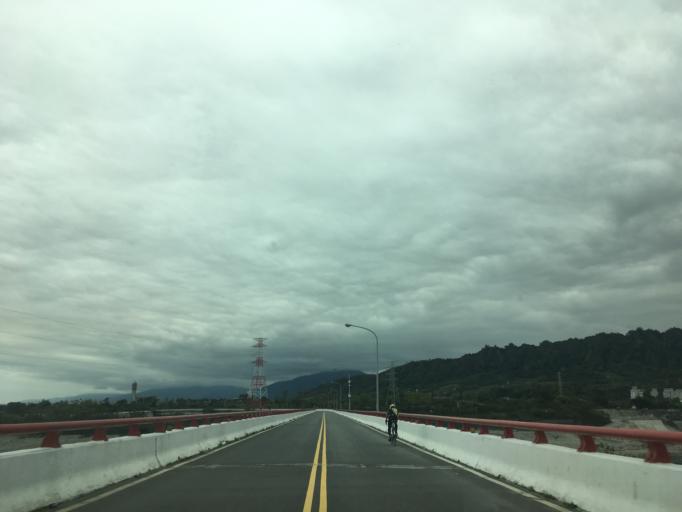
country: TW
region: Taiwan
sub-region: Taitung
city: Taitung
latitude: 22.8096
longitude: 121.1361
